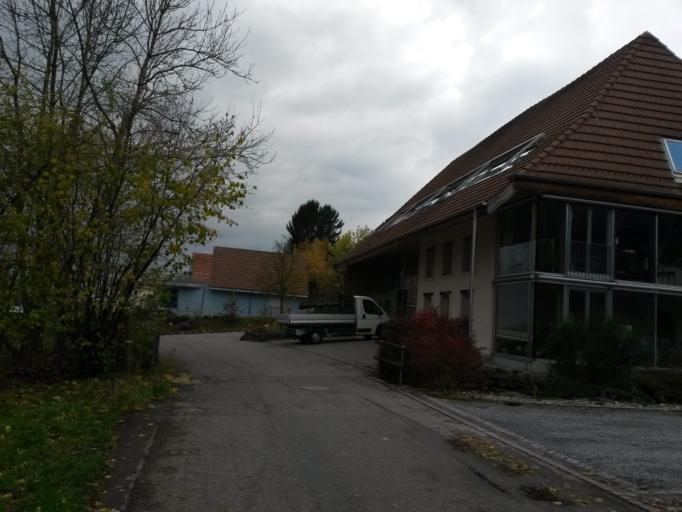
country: CH
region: Solothurn
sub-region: Bezirk Lebern
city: Bettlach
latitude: 47.2071
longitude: 7.4253
